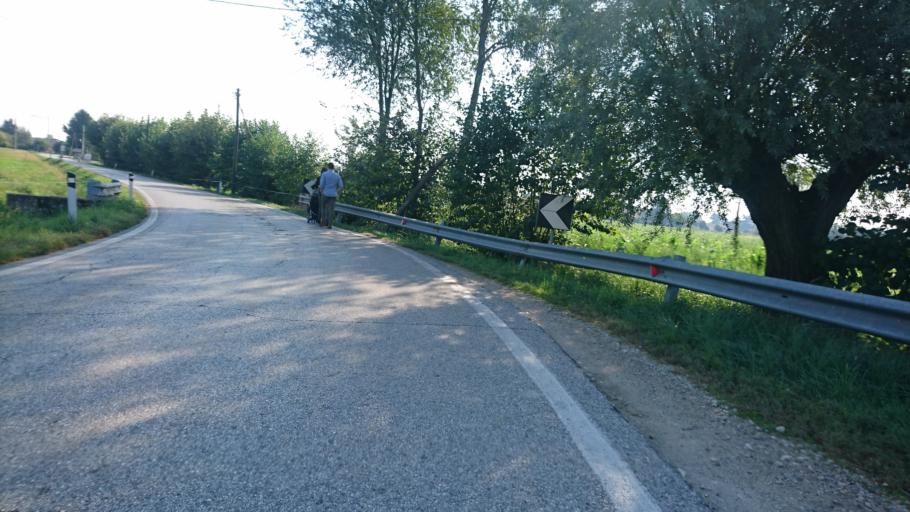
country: IT
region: Veneto
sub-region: Provincia di Padova
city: Gazzo
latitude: 45.5866
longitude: 11.7014
